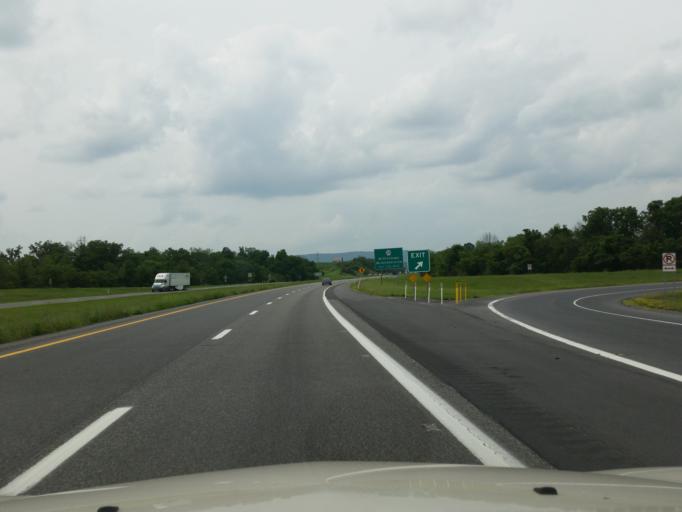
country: US
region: Pennsylvania
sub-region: Juniata County
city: Mifflintown
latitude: 40.5564
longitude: -77.3621
